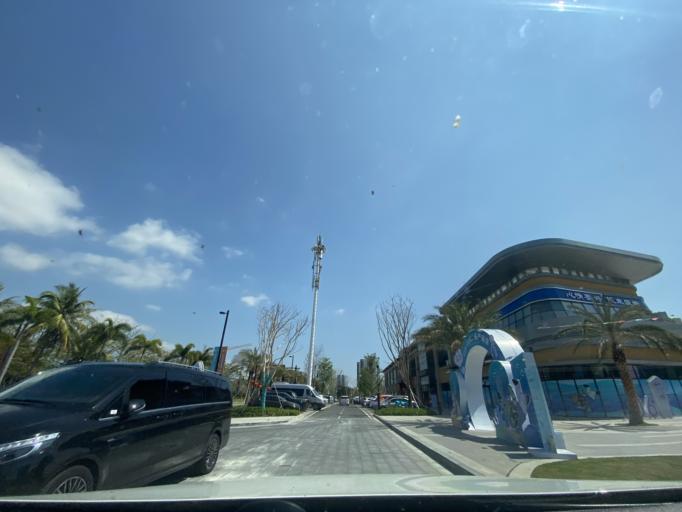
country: CN
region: Hainan
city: Xincun
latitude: 18.4197
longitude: 109.9114
